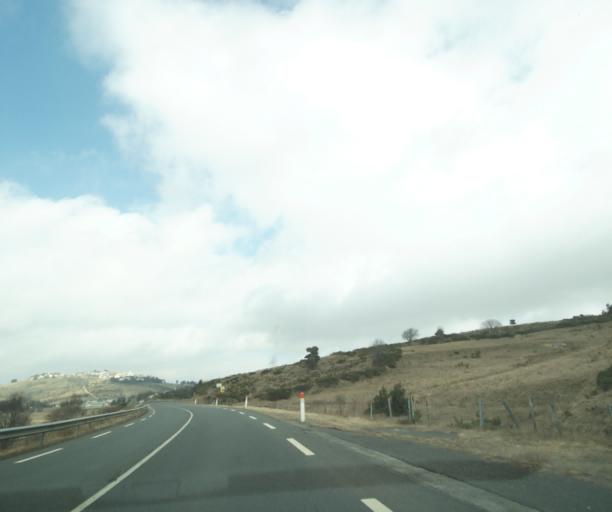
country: FR
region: Languedoc-Roussillon
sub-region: Departement de la Lozere
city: Mende
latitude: 44.6239
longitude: 3.6736
